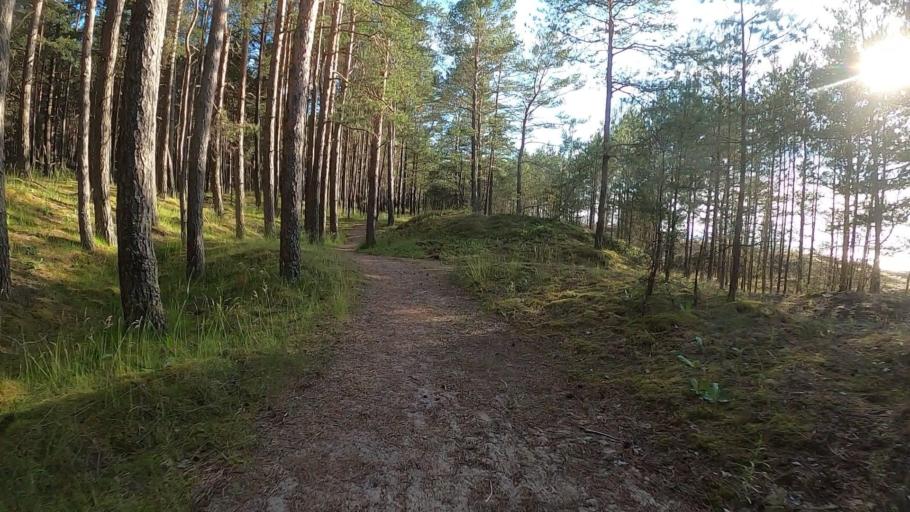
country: LV
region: Carnikava
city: Carnikava
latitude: 57.1197
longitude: 24.2031
